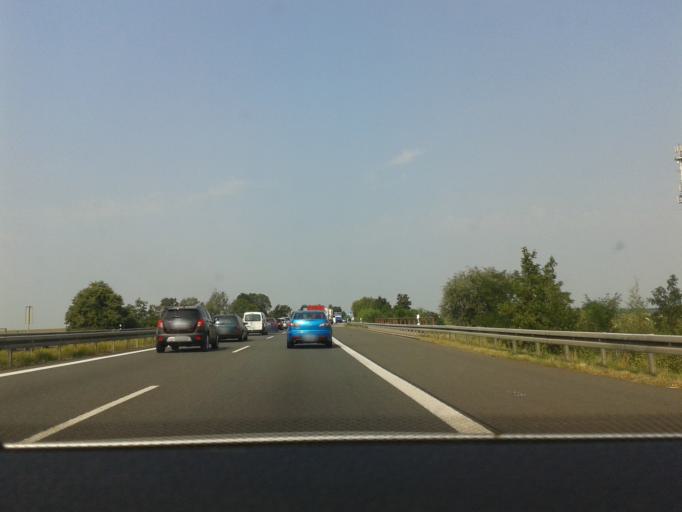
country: DE
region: Saxony
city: Grimma
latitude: 51.2577
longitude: 12.7204
